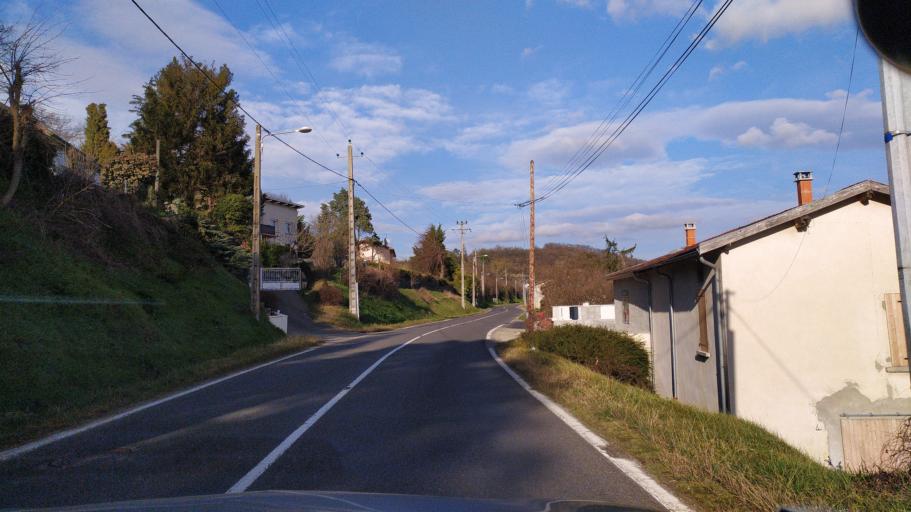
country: FR
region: Rhone-Alpes
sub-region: Departement de l'Isere
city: Pont-Eveque
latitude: 45.5415
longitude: 4.9168
